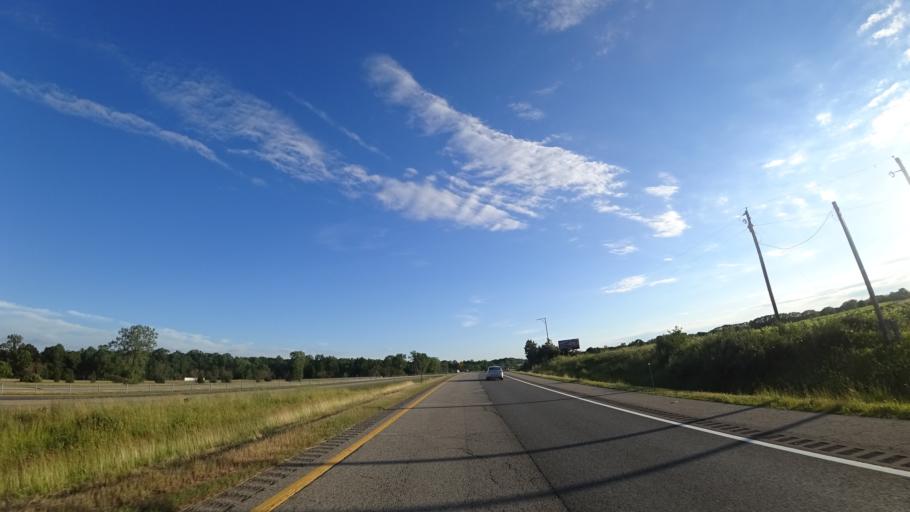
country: US
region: Michigan
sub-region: Berrien County
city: Benton Heights
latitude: 42.1331
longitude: -86.3710
